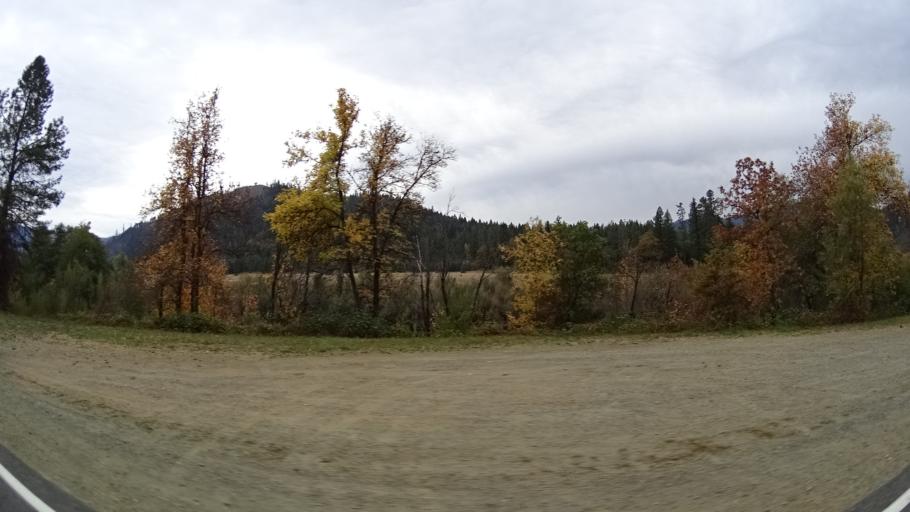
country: US
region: California
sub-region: Siskiyou County
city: Happy Camp
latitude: 41.8084
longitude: -123.3495
